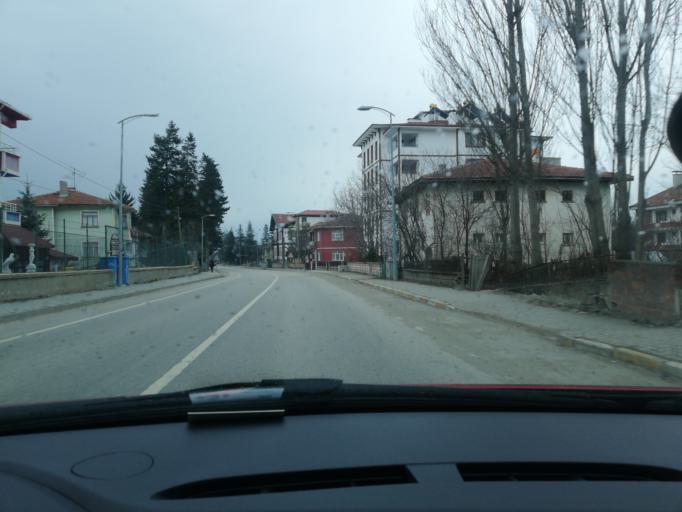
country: TR
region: Kastamonu
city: Daday
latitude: 41.4772
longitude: 33.4673
